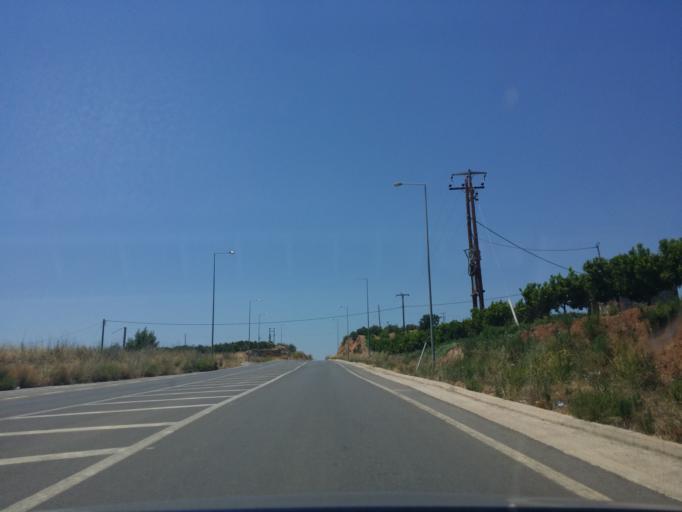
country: GR
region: Peloponnese
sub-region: Nomos Lakonias
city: Kato Glikovrisi
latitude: 36.8527
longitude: 22.7690
